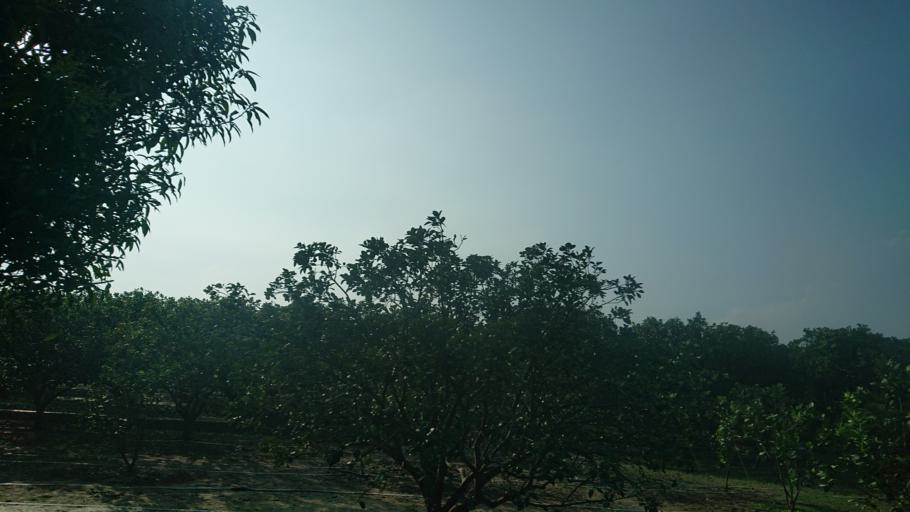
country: TW
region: Taiwan
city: Xinying
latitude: 23.1610
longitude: 120.2502
